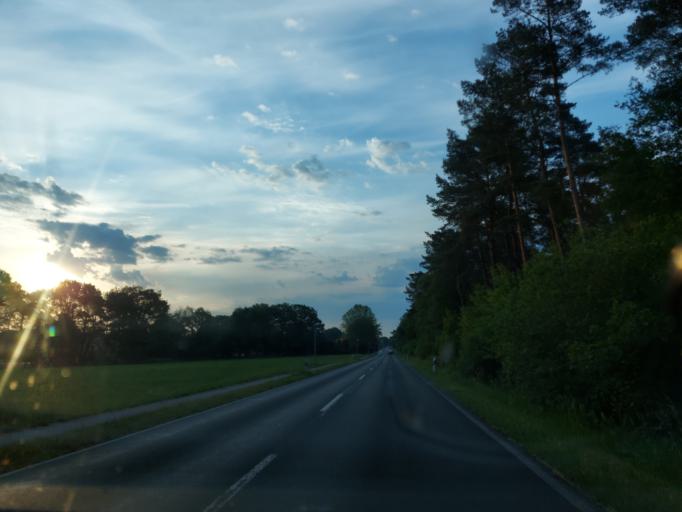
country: DE
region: North Rhine-Westphalia
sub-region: Regierungsbezirk Detmold
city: Verl
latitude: 51.9363
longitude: 8.4580
